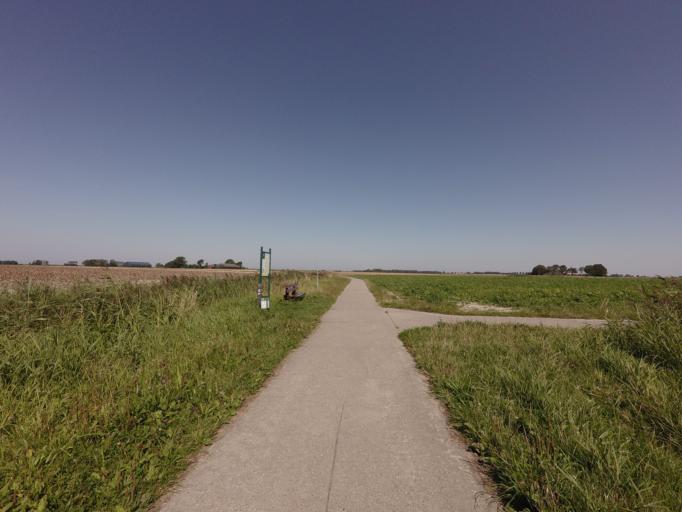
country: NL
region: Friesland
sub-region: Gemeente Dongeradeel
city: Anjum
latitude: 53.3873
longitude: 6.0657
